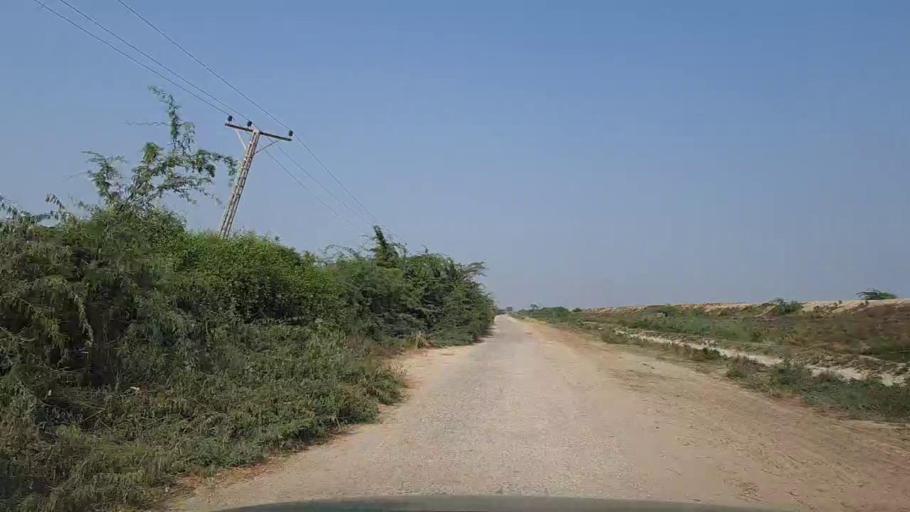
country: PK
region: Sindh
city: Chuhar Jamali
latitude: 24.5173
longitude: 67.9254
